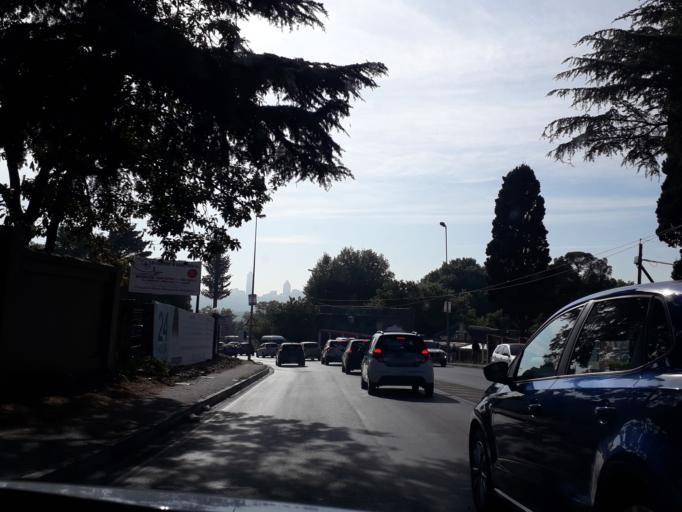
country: ZA
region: Gauteng
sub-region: City of Johannesburg Metropolitan Municipality
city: Johannesburg
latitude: -26.1005
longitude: 28.0042
